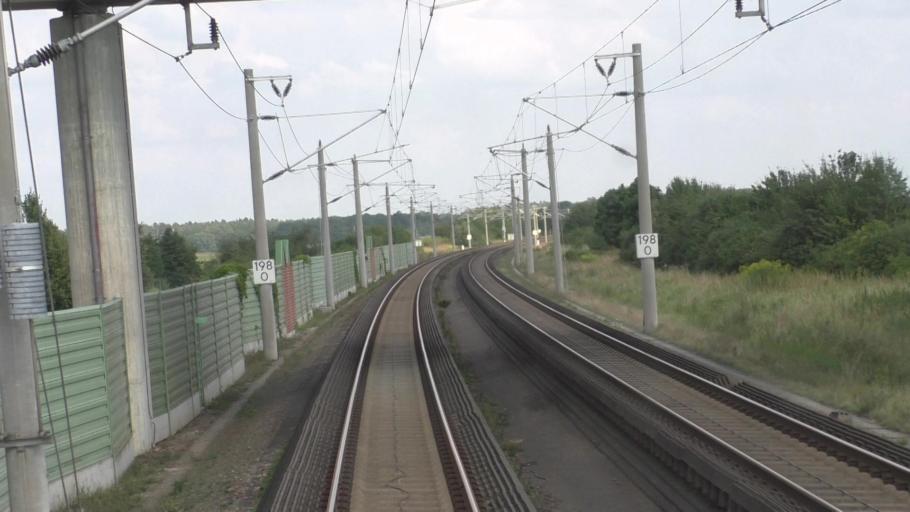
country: DE
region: Saxony-Anhalt
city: Hassel
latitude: 52.5997
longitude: 11.9570
